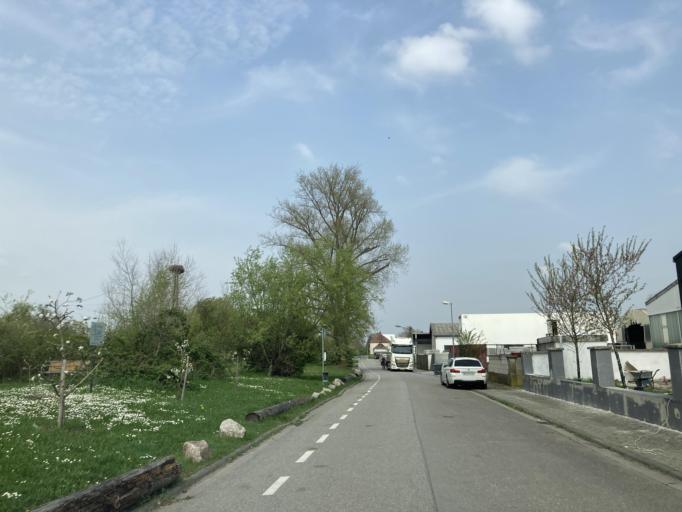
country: DE
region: Baden-Wuerttemberg
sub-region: Karlsruhe Region
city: Kronau
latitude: 49.2147
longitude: 8.6463
